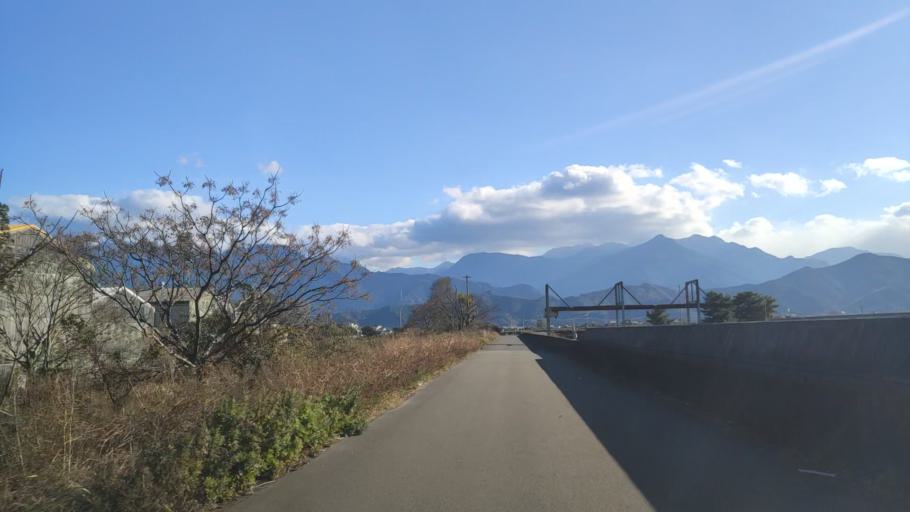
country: JP
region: Ehime
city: Saijo
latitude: 33.9221
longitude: 133.1558
